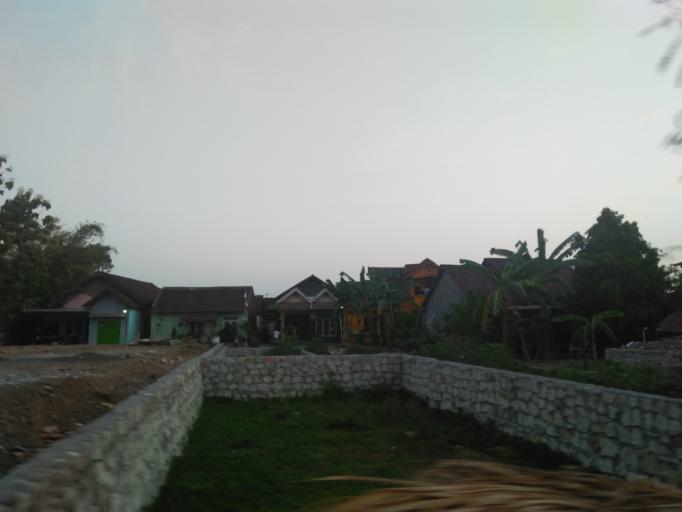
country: ID
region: Daerah Istimewa Yogyakarta
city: Sewon
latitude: -7.8435
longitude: 110.3925
